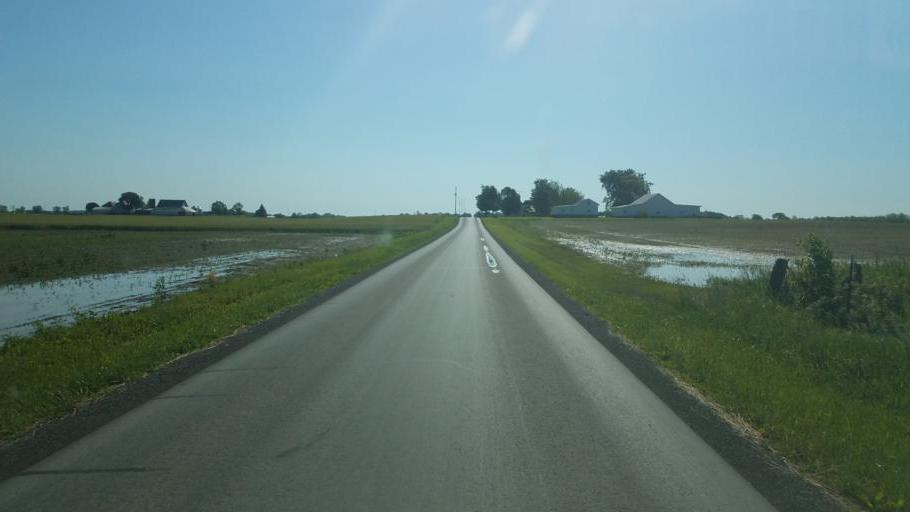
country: US
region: Ohio
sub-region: Hardin County
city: Kenton
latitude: 40.5952
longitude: -83.6014
